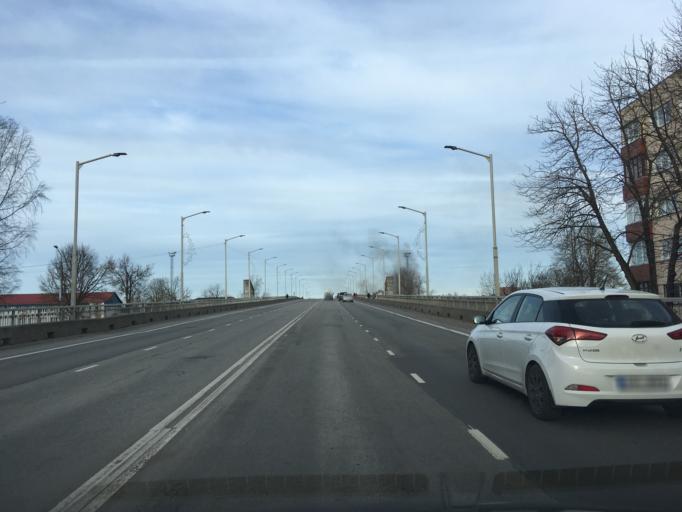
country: EE
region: Ida-Virumaa
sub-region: Narva linn
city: Narva
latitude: 59.3698
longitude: 28.1851
